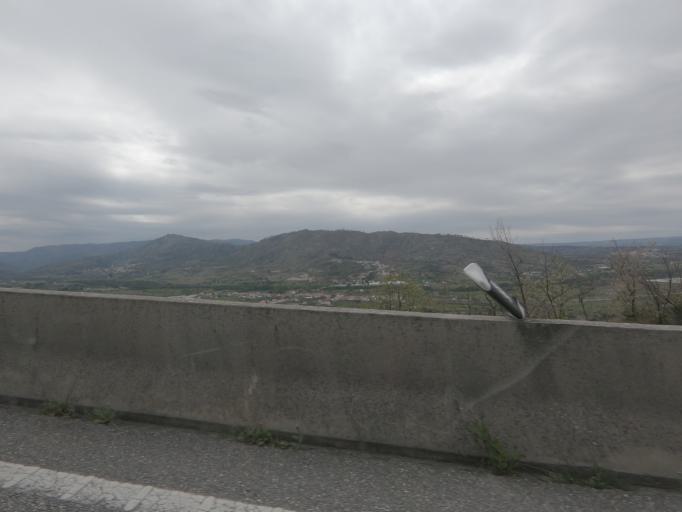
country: PT
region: Guarda
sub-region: Guarda
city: Guarda
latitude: 40.6097
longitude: -7.2831
